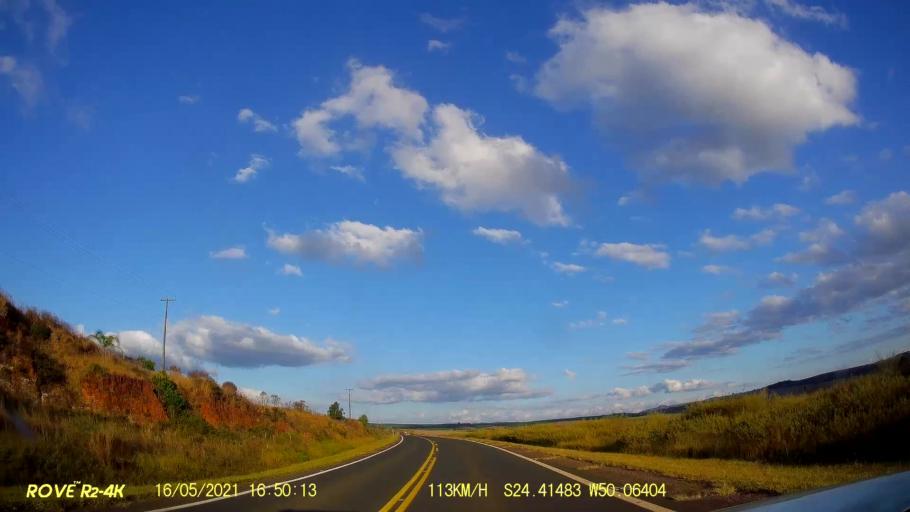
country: BR
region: Parana
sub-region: Pirai Do Sul
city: Pirai do Sul
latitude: -24.4144
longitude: -50.0643
